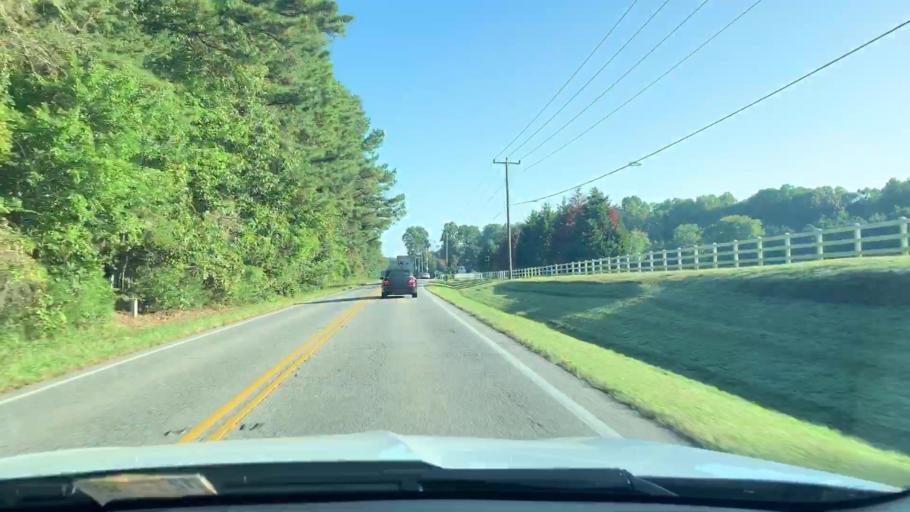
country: US
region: Virginia
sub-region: Middlesex County
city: Deltaville
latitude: 37.5265
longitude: -76.4230
